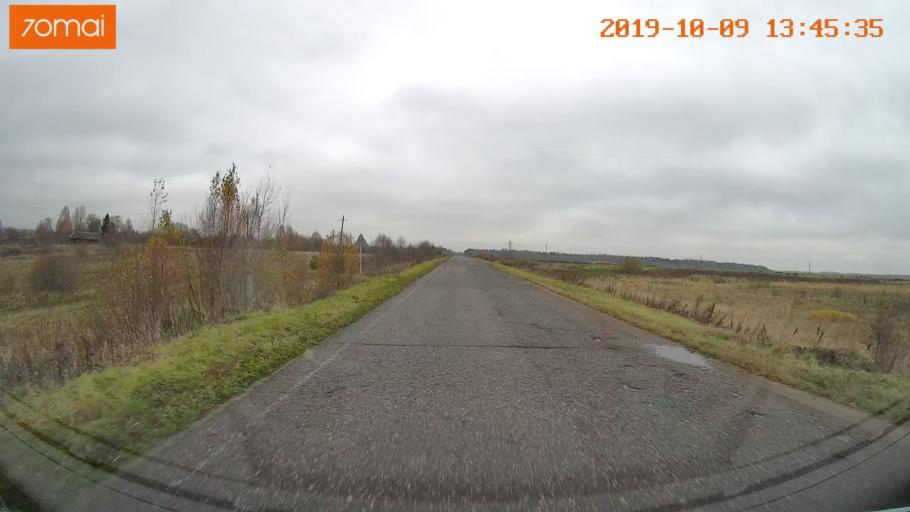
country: RU
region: Kostroma
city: Buy
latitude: 58.3756
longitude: 41.2110
